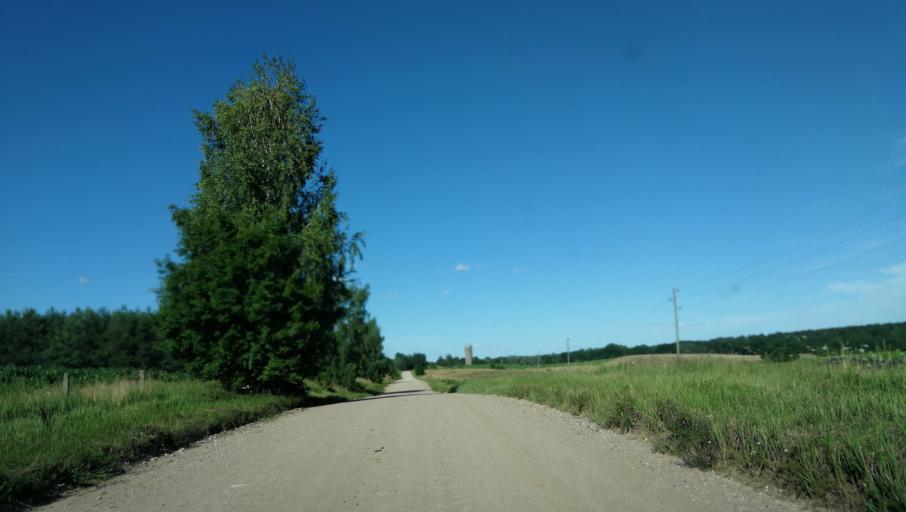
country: LV
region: Jaunpiebalga
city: Jaunpiebalga
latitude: 57.0097
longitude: 26.0413
